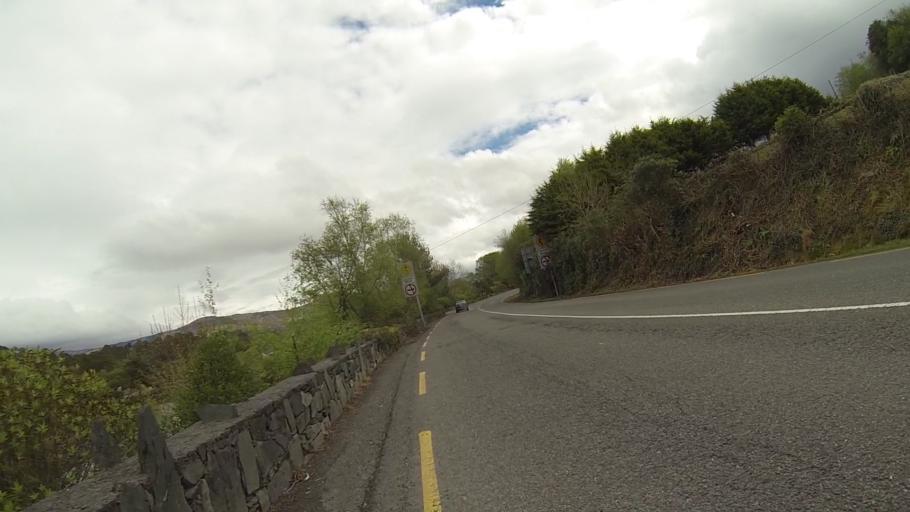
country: IE
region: Munster
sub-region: County Cork
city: Bantry
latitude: 51.7465
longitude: -9.5529
